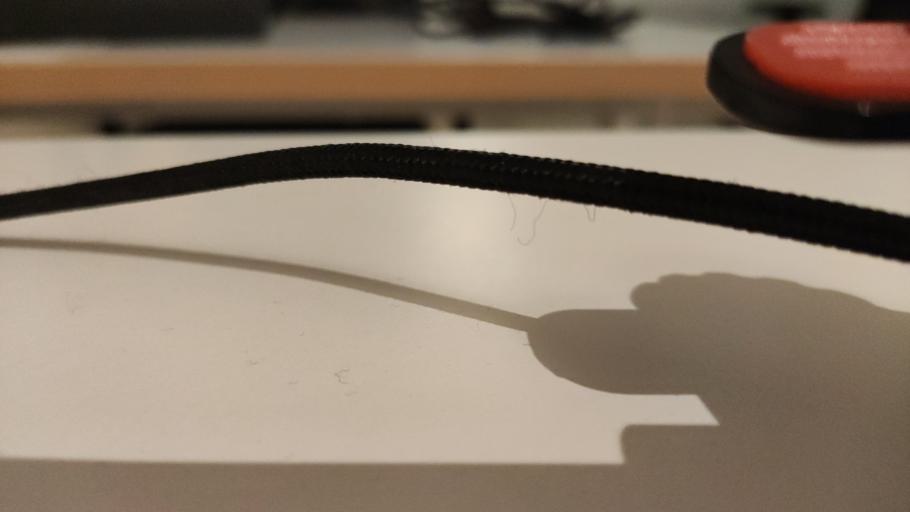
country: RU
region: Moskovskaya
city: Kurovskoye
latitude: 55.6046
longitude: 38.9269
